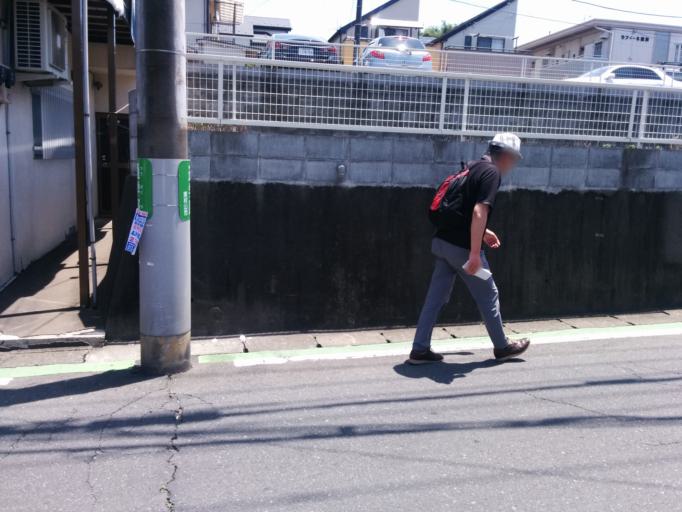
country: JP
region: Tokyo
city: Higashimurayama-shi
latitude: 35.7672
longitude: 139.4670
